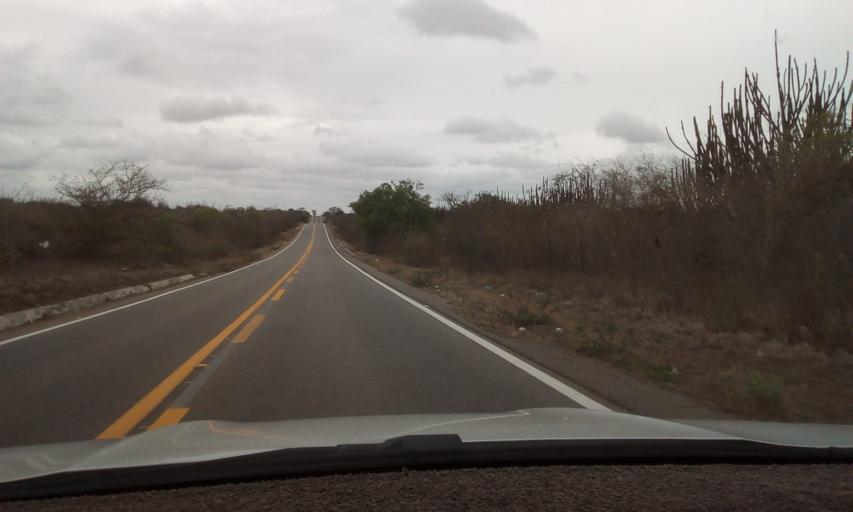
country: BR
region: Paraiba
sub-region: Areia
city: Remigio
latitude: -6.9099
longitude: -35.8669
